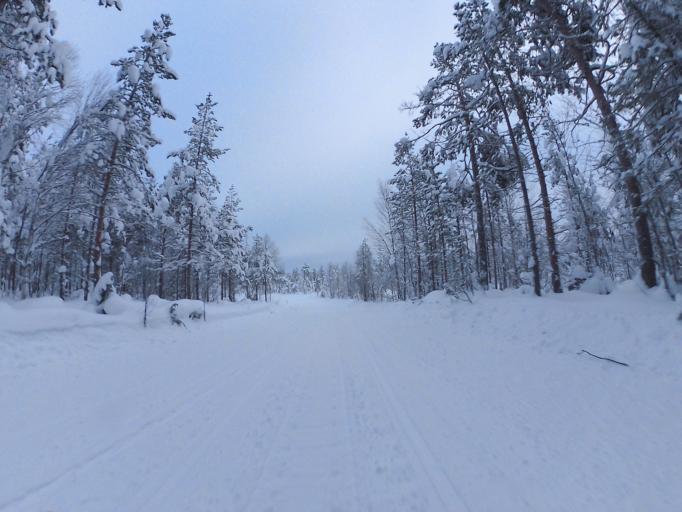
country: FI
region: Lapland
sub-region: Rovaniemi
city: Rovaniemi
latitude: 66.6268
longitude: 26.0352
